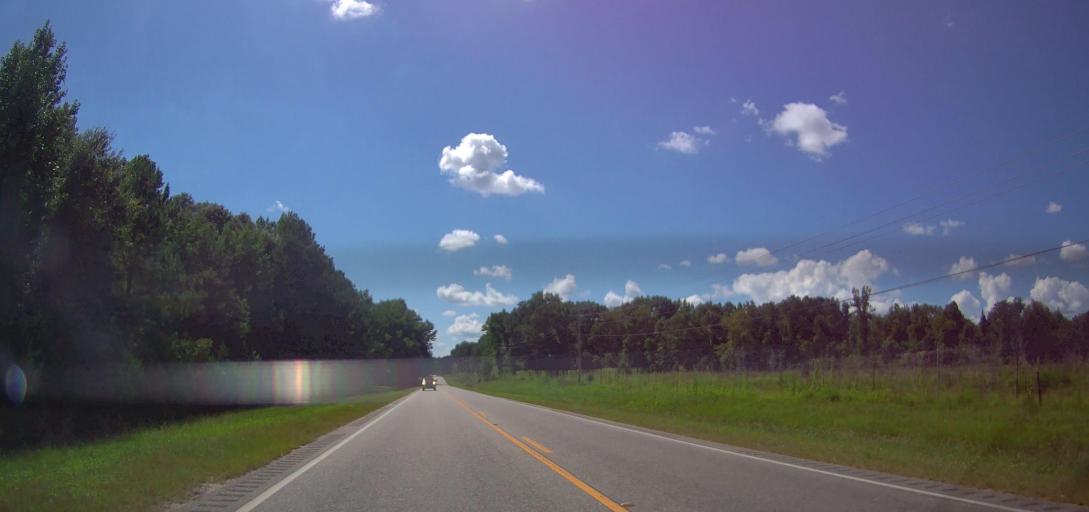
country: US
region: Alabama
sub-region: Macon County
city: Tuskegee
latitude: 32.3819
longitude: -85.8026
